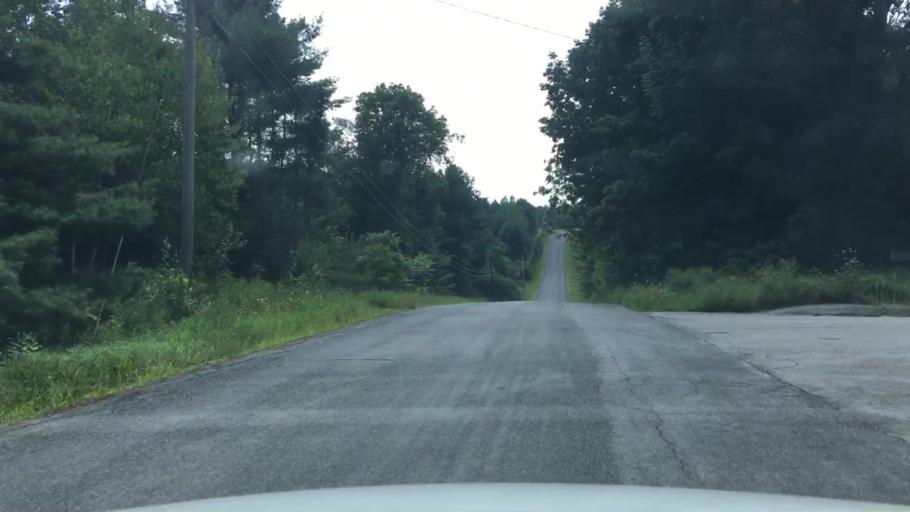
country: US
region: Maine
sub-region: Kennebec County
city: Manchester
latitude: 44.3663
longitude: -69.8162
